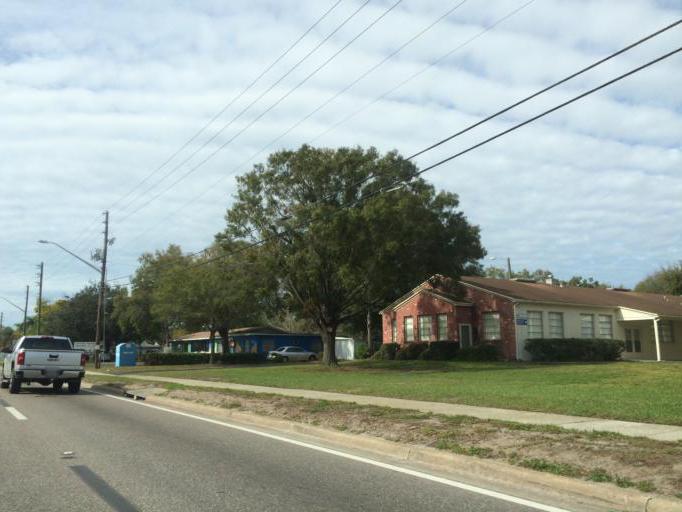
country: US
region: Florida
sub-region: Pinellas County
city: West and East Lealman
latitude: 27.8065
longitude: -82.6921
